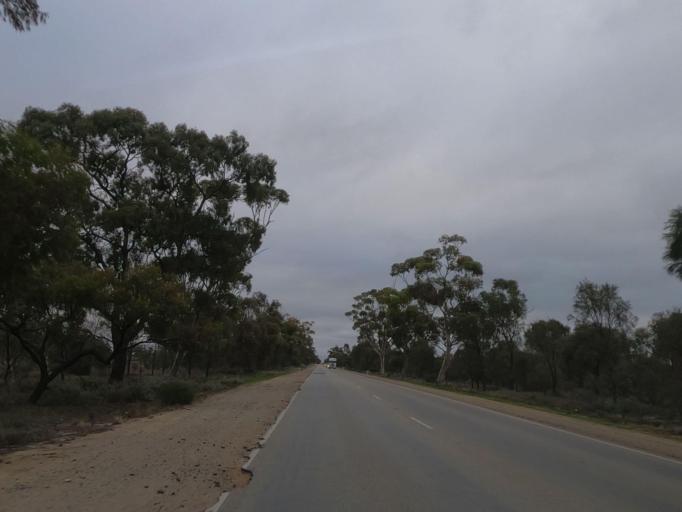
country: AU
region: Victoria
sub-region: Swan Hill
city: Swan Hill
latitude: -35.4109
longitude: 143.5855
